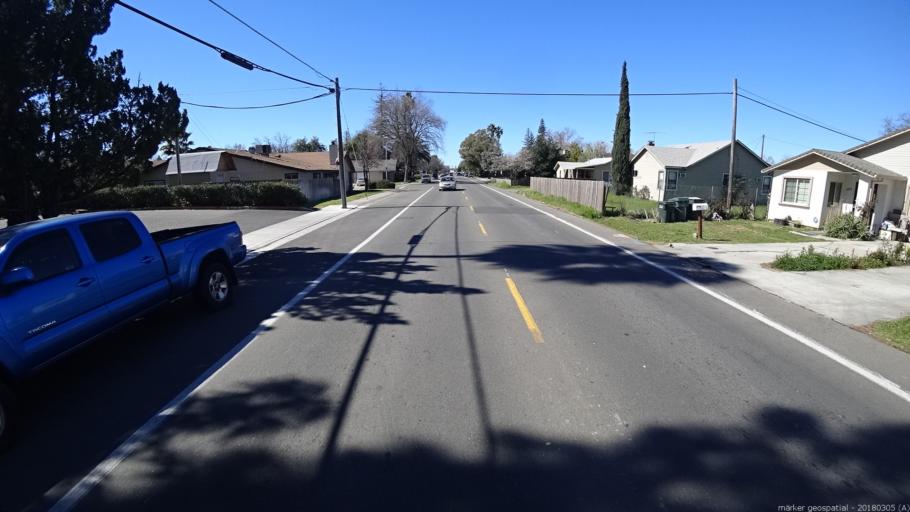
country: US
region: California
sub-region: Sacramento County
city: Florin
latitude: 38.4924
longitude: -121.4316
